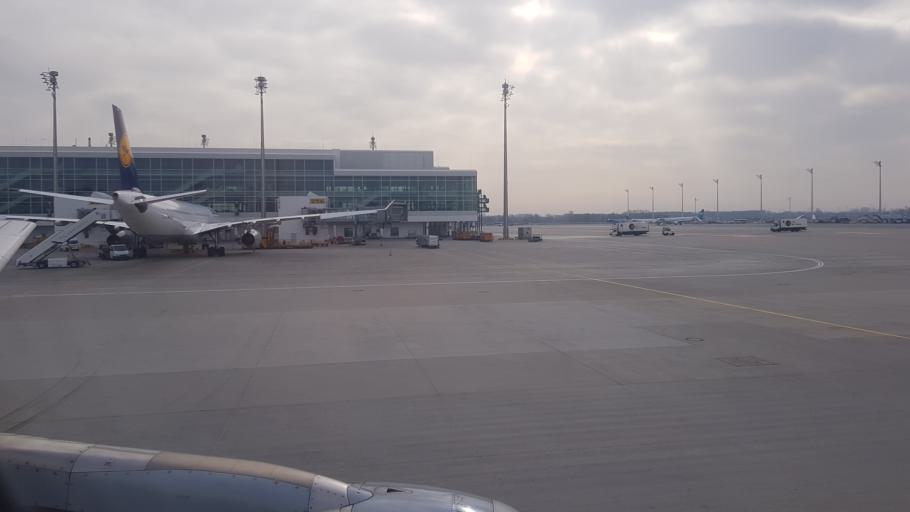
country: DE
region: Bavaria
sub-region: Upper Bavaria
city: Hallbergmoos
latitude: 48.3522
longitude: 11.7960
